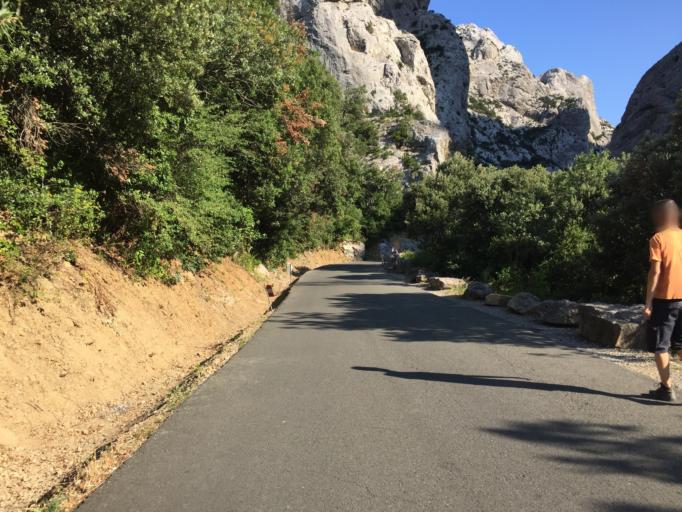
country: FR
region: Languedoc-Roussillon
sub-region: Departement des Pyrenees-Orientales
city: Saint-Paul-de-Fenouillet
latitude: 42.8458
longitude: 2.4779
